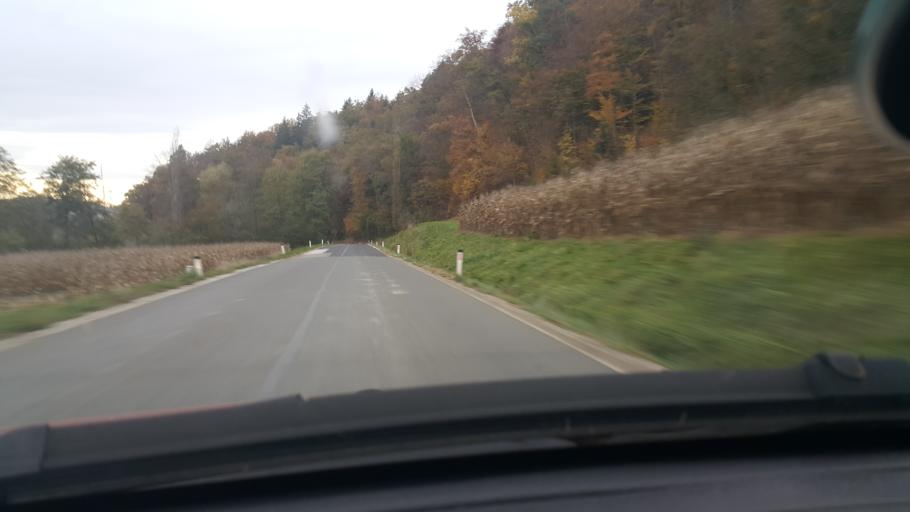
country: SI
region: Kungota
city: Zgornja Kungota
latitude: 46.6430
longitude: 15.5842
